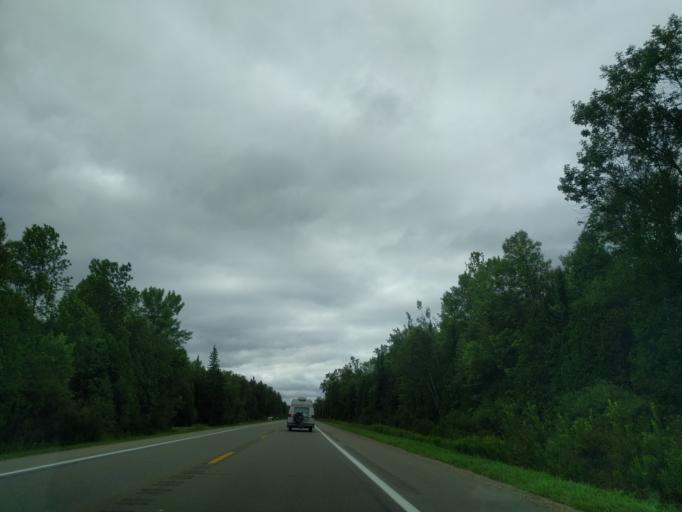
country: US
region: Michigan
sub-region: Menominee County
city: Menominee
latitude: 45.3154
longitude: -87.4343
